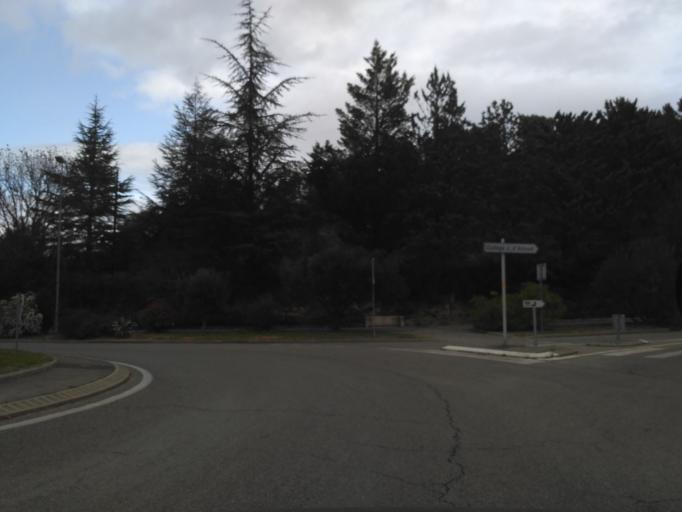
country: FR
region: Provence-Alpes-Cote d'Azur
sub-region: Departement du Var
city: Barjols
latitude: 43.5626
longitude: 6.0088
